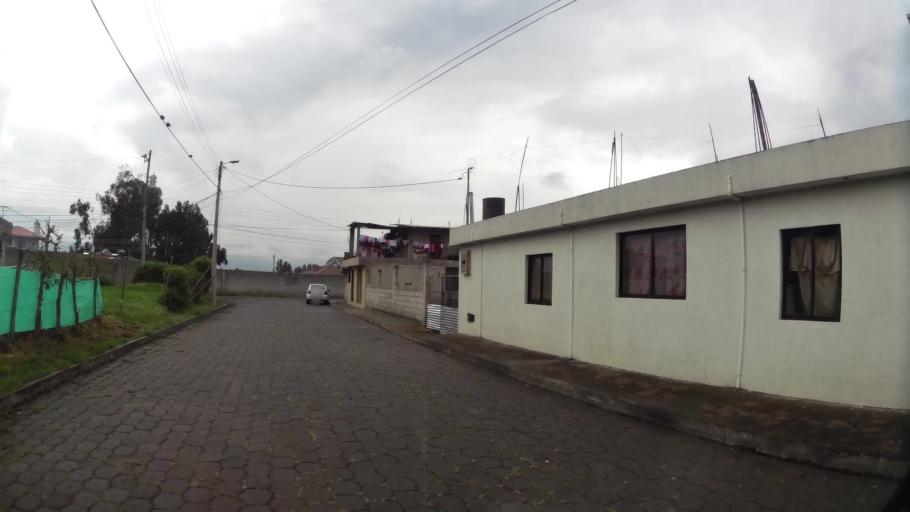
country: EC
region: Pichincha
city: Sangolqui
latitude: -0.3186
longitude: -78.4346
